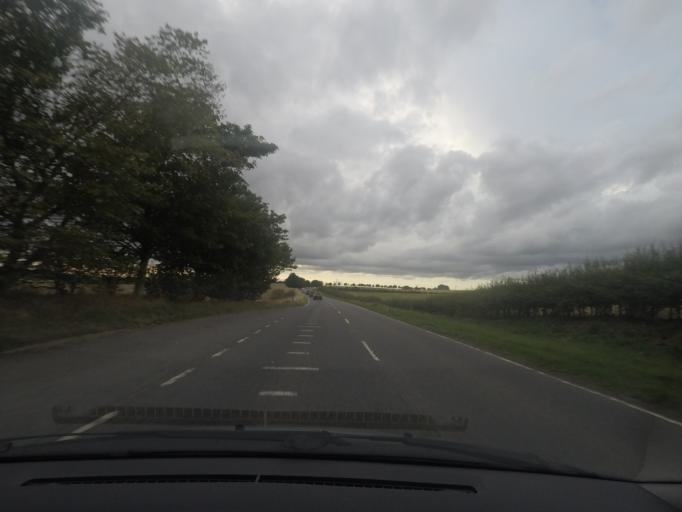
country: GB
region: England
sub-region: Lincolnshire
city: Burwell
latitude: 53.3071
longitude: 0.0207
